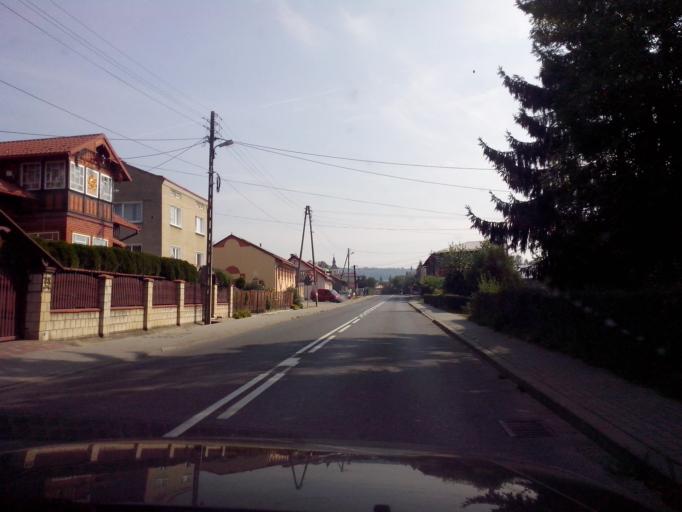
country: PL
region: Subcarpathian Voivodeship
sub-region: Powiat strzyzowski
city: Czudec
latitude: 49.9455
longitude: 21.8288
